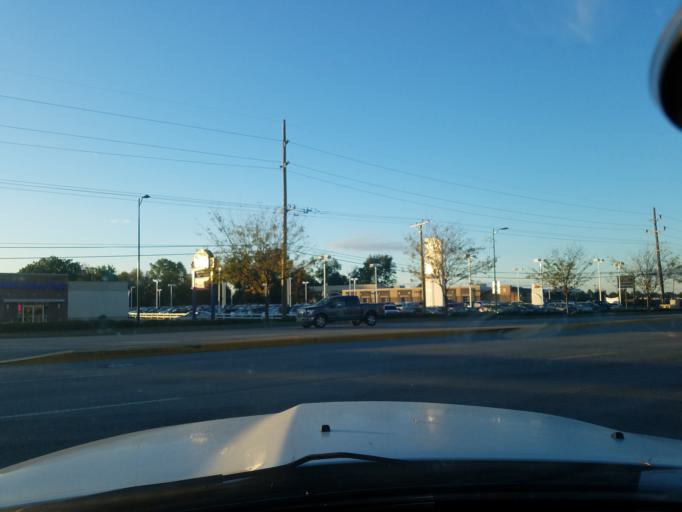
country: US
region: Indiana
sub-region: Clark County
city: Clarksville
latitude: 38.3144
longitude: -85.7618
